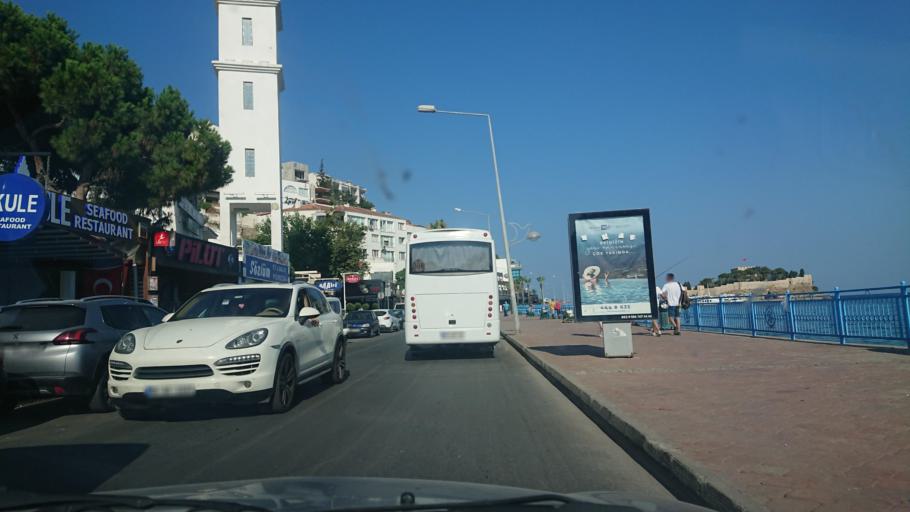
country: TR
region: Aydin
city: Kusadasi
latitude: 37.8608
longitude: 27.2539
